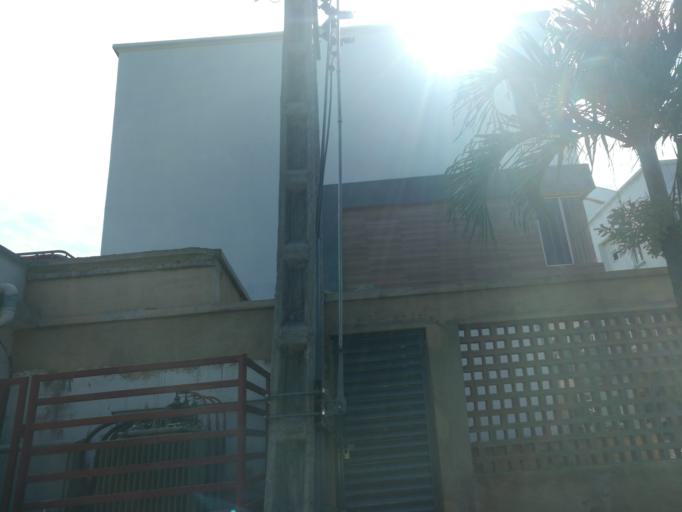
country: NG
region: Lagos
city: Ojota
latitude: 6.5763
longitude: 3.3647
